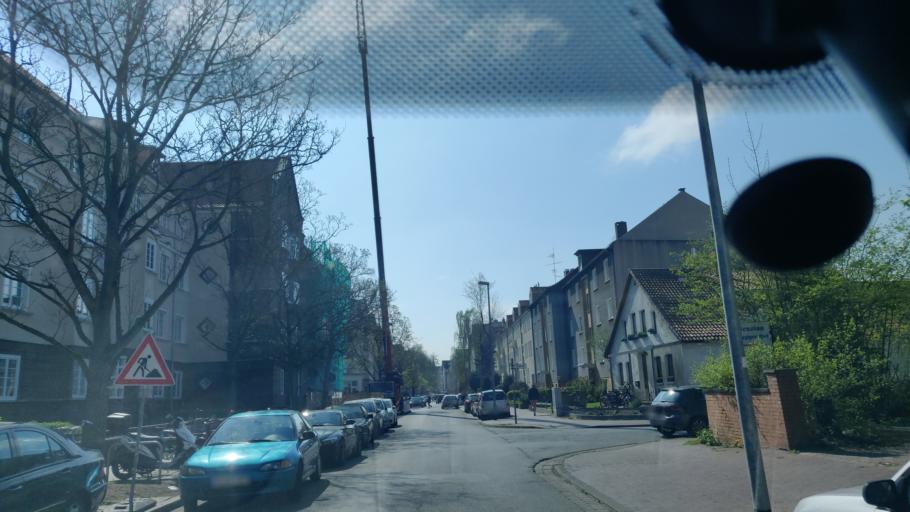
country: DE
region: Lower Saxony
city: Hannover
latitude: 52.3409
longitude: 9.7597
